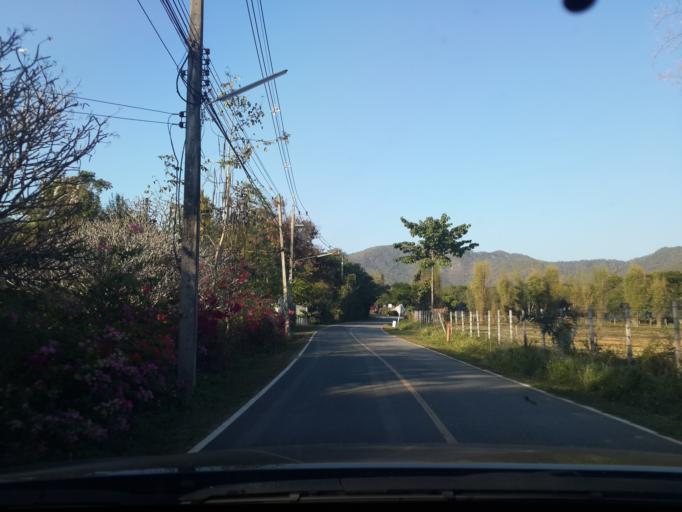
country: TH
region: Chiang Mai
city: San Sai
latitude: 18.9223
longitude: 99.1376
